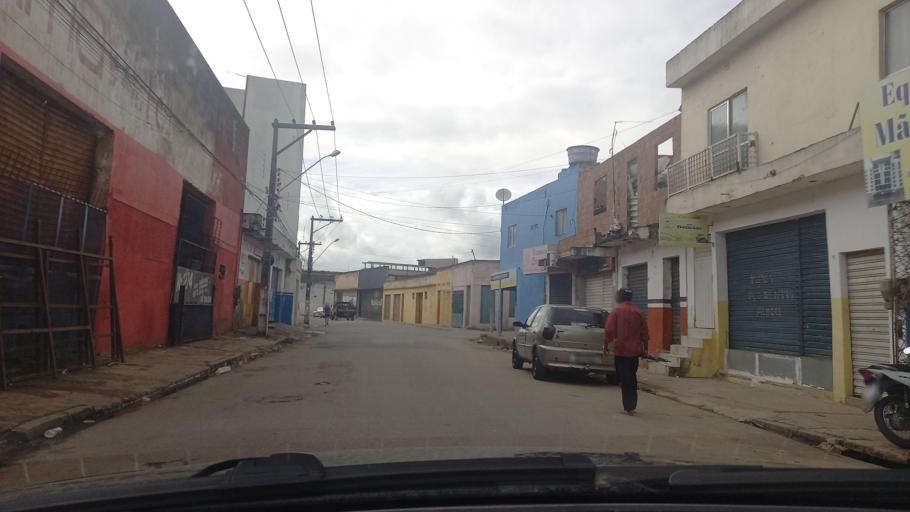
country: BR
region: Pernambuco
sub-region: Vitoria De Santo Antao
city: Vitoria de Santo Antao
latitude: -8.1183
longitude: -35.2995
